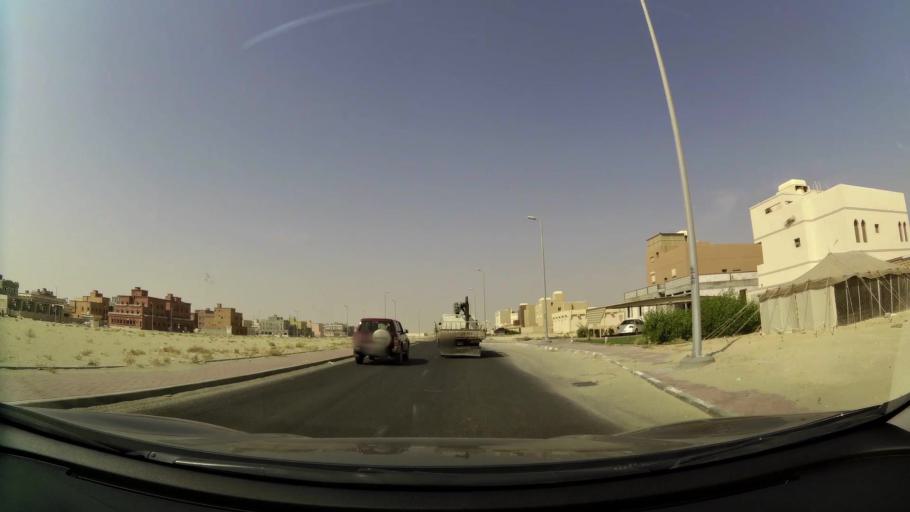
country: KW
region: Al Ahmadi
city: Al Wafrah
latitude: 28.7998
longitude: 48.0554
